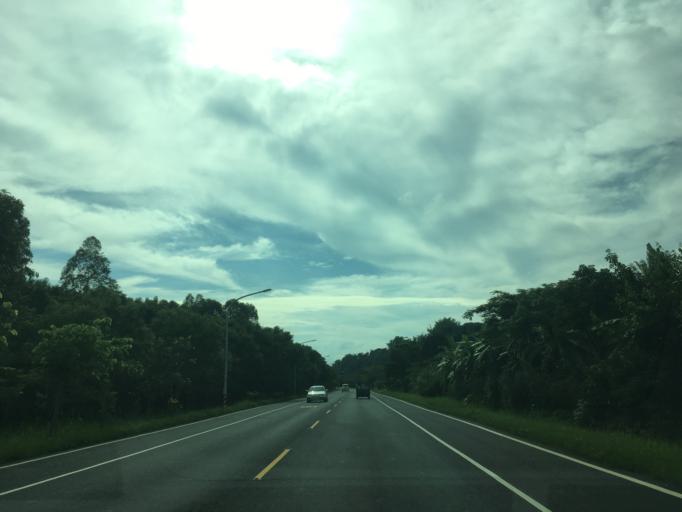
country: TW
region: Taiwan
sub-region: Chiayi
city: Jiayi Shi
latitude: 23.4513
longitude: 120.5678
